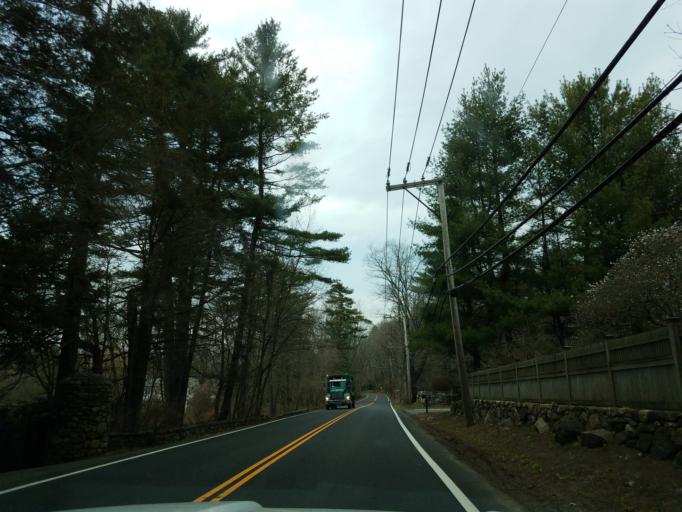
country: US
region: Connecticut
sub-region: Fairfield County
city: Glenville
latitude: 41.0677
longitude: -73.6394
